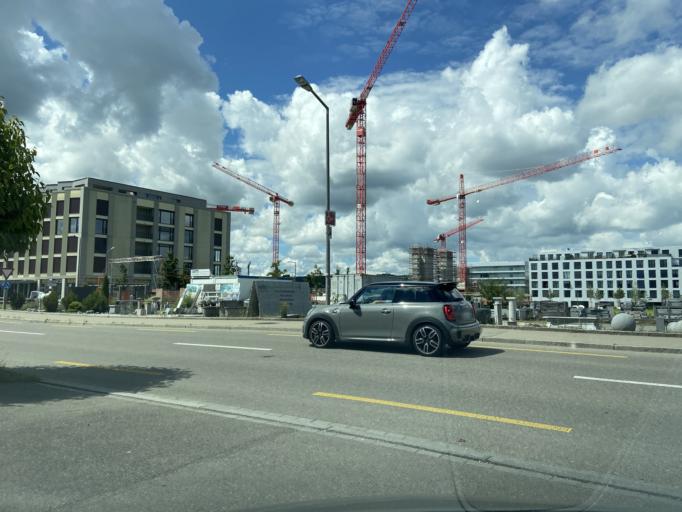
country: CH
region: Zurich
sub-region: Bezirk Winterthur
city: Oberwinterthur (Kreis 2) / Hegi
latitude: 47.5039
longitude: 8.7690
